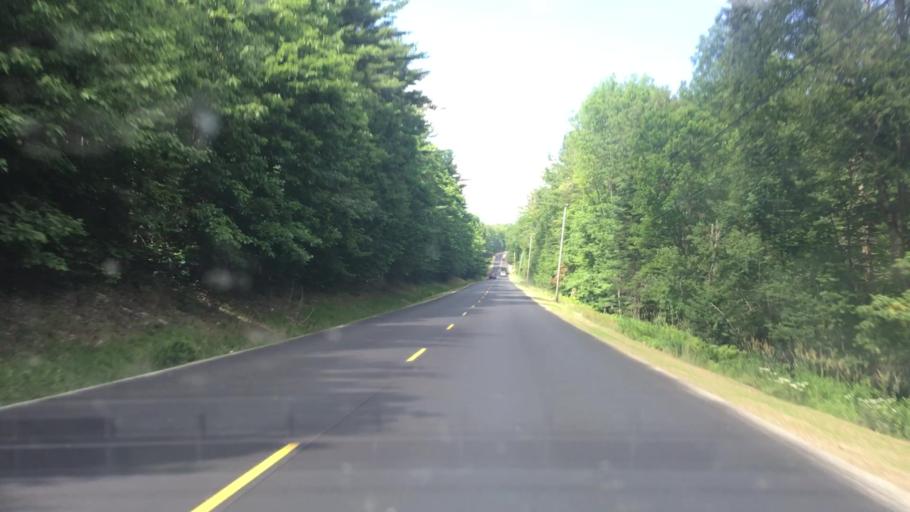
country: US
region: Maine
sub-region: Franklin County
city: Jay
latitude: 44.5417
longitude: -70.1893
